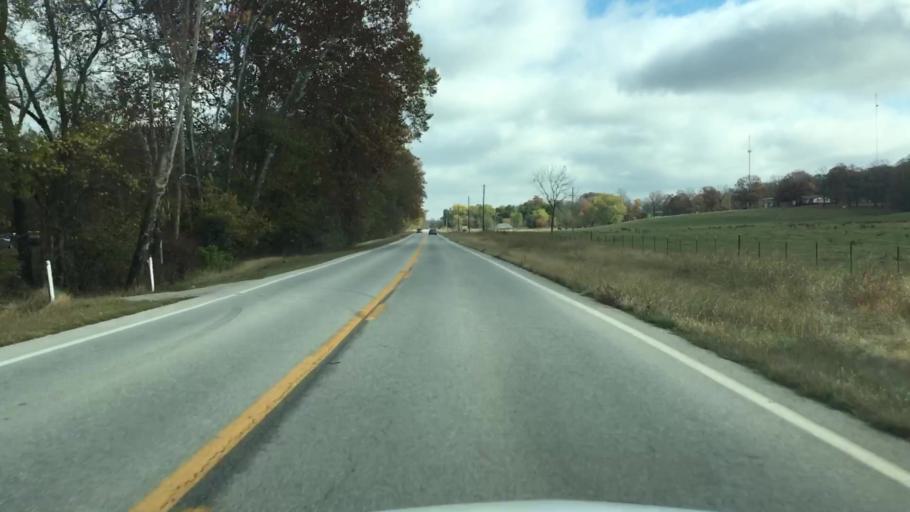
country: US
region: Arkansas
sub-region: Benton County
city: Gentry
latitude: 36.2575
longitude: -94.4016
